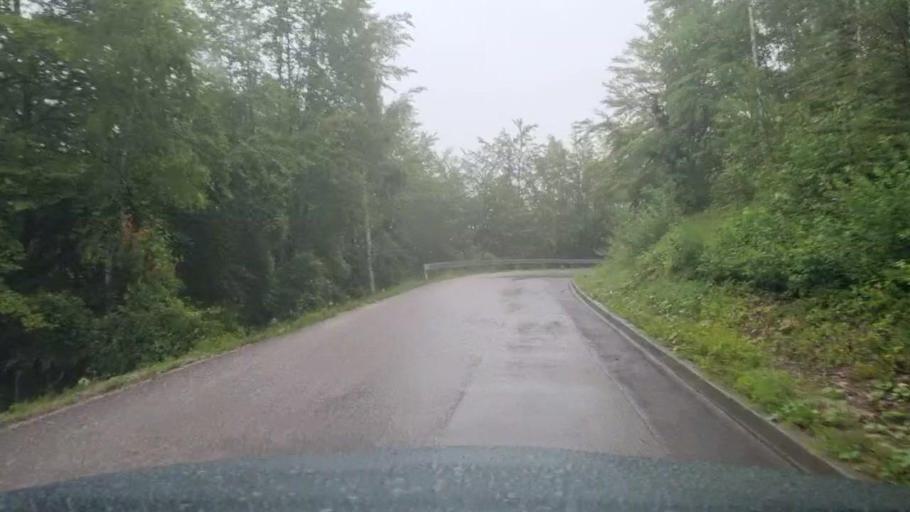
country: BA
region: Federation of Bosnia and Herzegovina
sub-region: Bosansko-Podrinjski Kanton
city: Ustikolina
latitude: 43.6329
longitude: 18.6249
